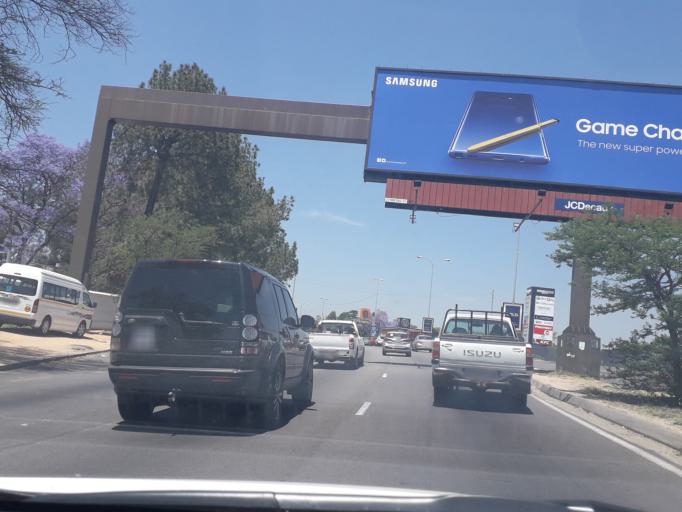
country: ZA
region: Gauteng
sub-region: City of Johannesburg Metropolitan Municipality
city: Diepsloot
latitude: -26.0414
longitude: 28.0148
